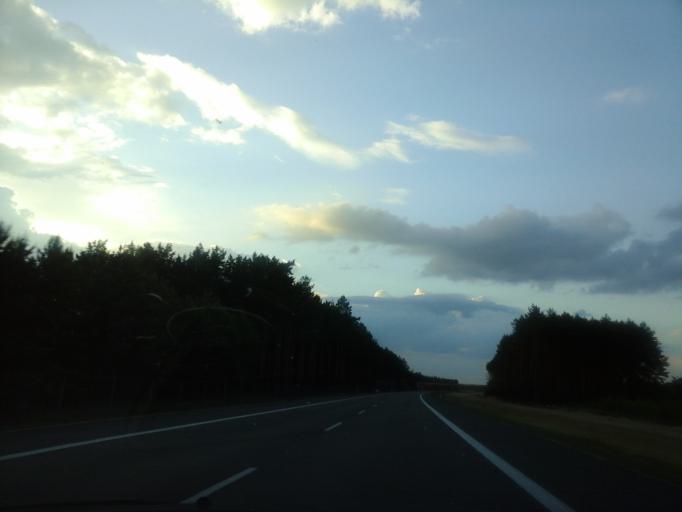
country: PL
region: Lubusz
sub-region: Powiat nowosolski
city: Otyn
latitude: 51.8212
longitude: 15.6749
